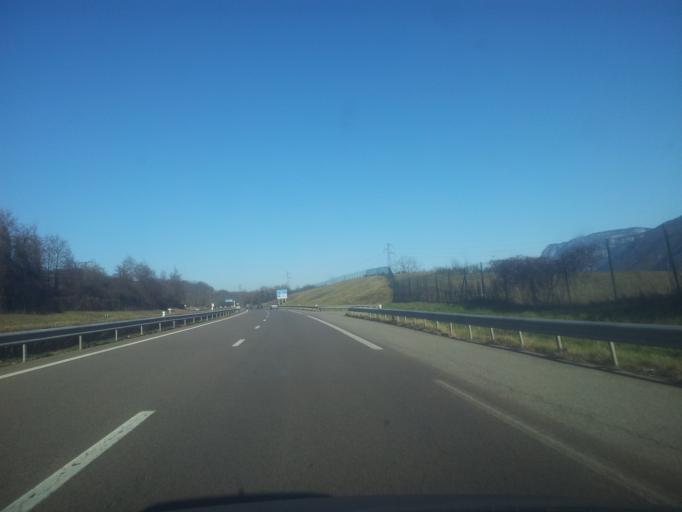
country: FR
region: Rhone-Alpes
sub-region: Departement de l'Isere
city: Saint-Sauveur
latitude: 45.1523
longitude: 5.3565
